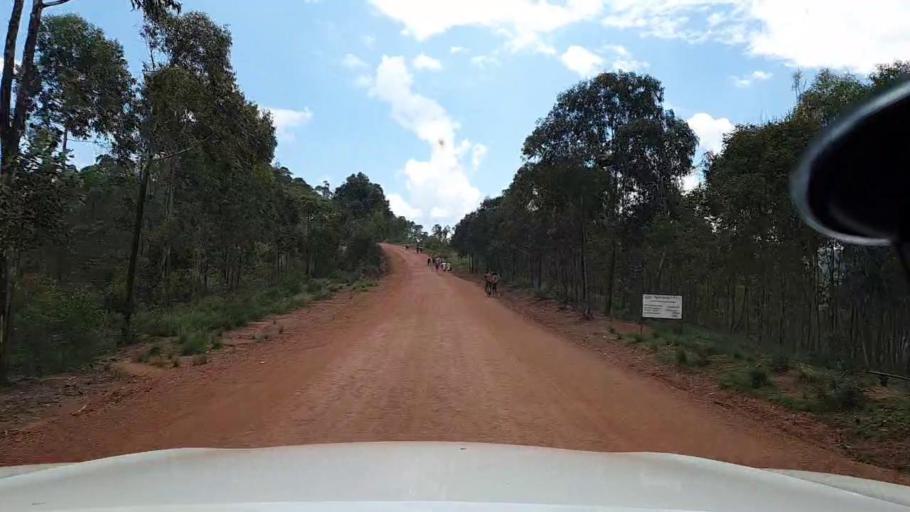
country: RW
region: Kigali
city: Kigali
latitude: -1.7634
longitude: 29.8415
